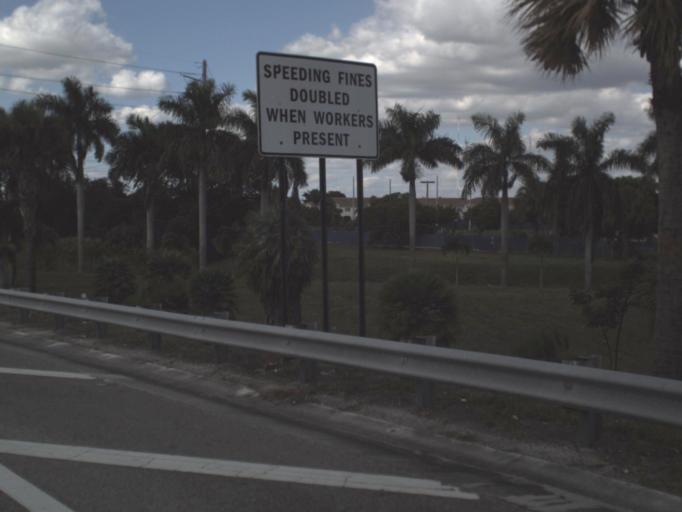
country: US
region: Florida
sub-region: Miami-Dade County
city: Norland
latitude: 25.9309
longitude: -80.2115
